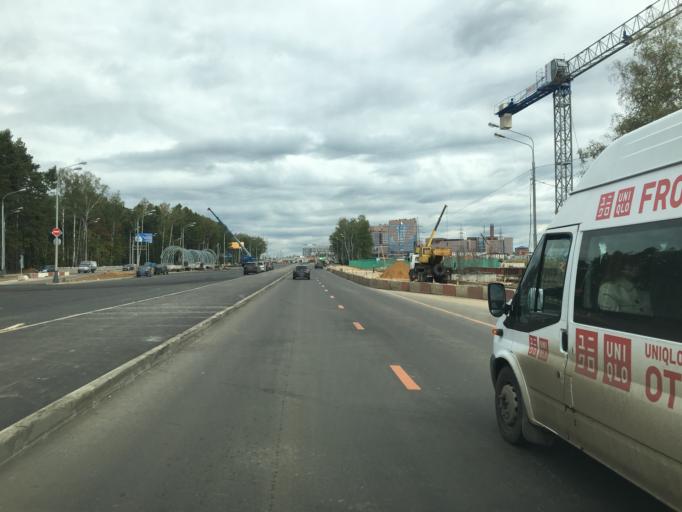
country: RU
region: Moskovskaya
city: Kommunarka
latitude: 55.5759
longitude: 37.4599
